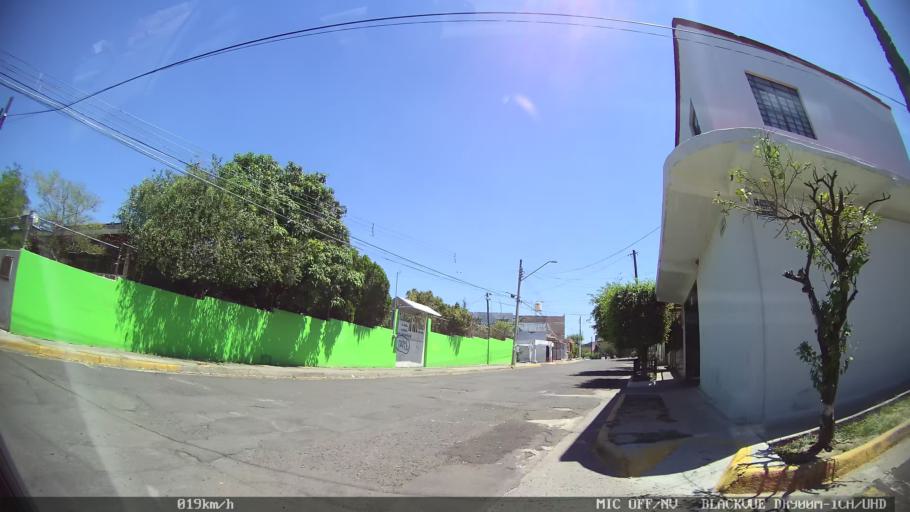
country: MX
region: Jalisco
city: Tlaquepaque
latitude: 20.6690
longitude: -103.2714
